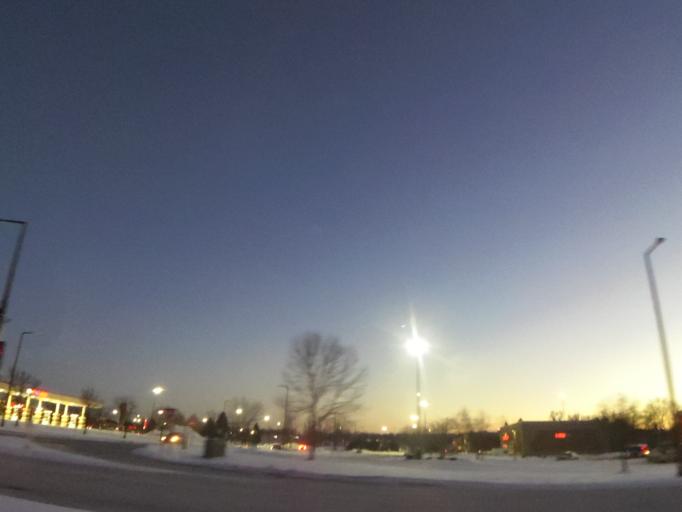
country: US
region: Minnesota
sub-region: Washington County
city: Stillwater
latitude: 45.0397
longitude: -92.8413
